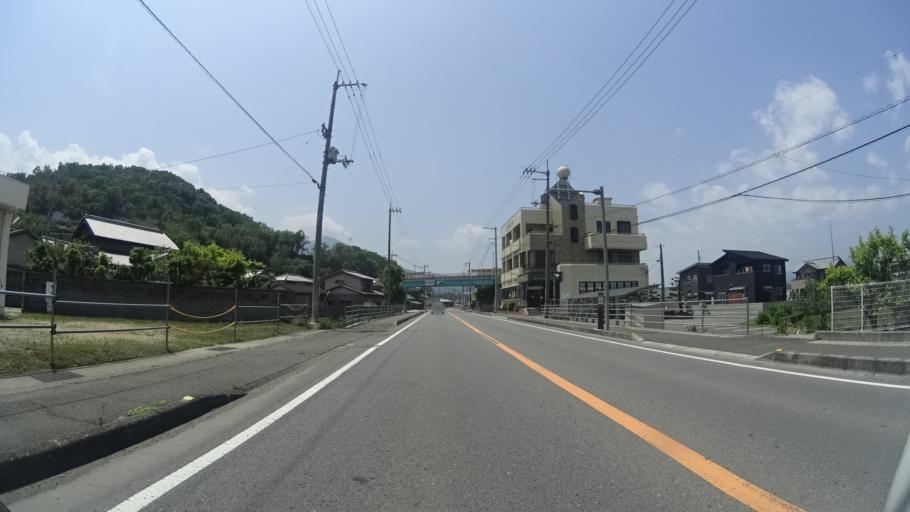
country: JP
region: Tokushima
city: Kamojimacho-jogejima
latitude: 34.0605
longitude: 134.2530
